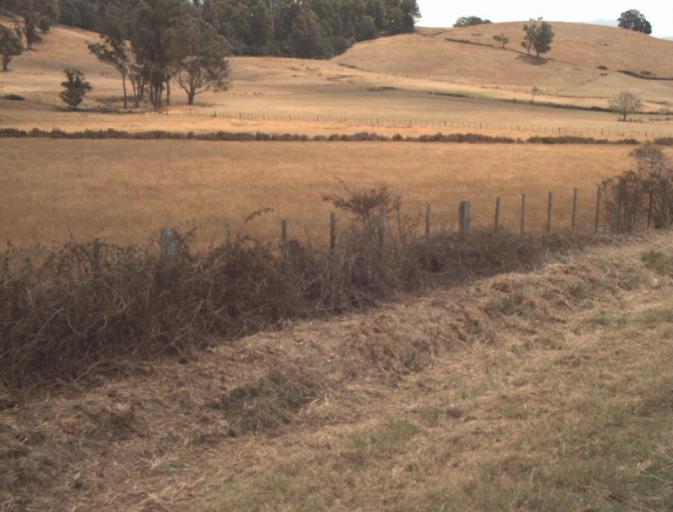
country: AU
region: Tasmania
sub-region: Launceston
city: Mayfield
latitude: -41.2466
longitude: 147.1417
